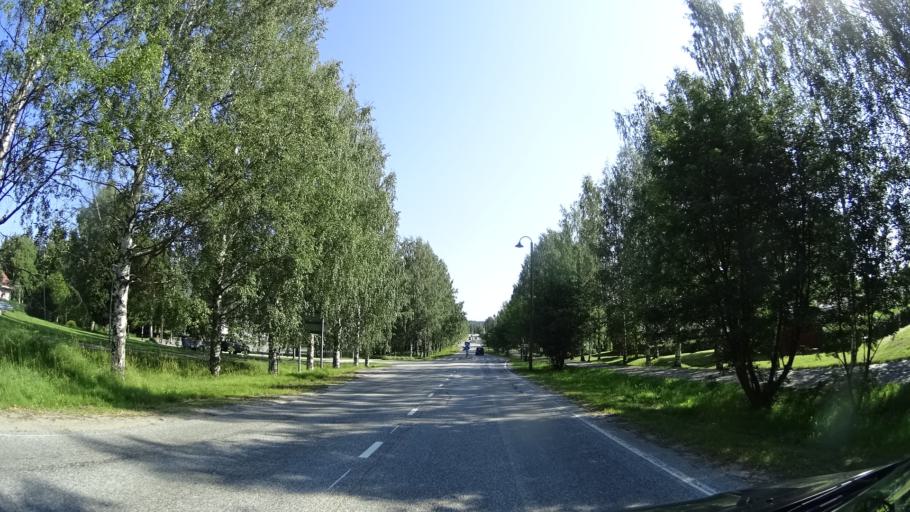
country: FI
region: North Karelia
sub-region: Joensuu
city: Juuka
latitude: 63.2441
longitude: 29.2567
